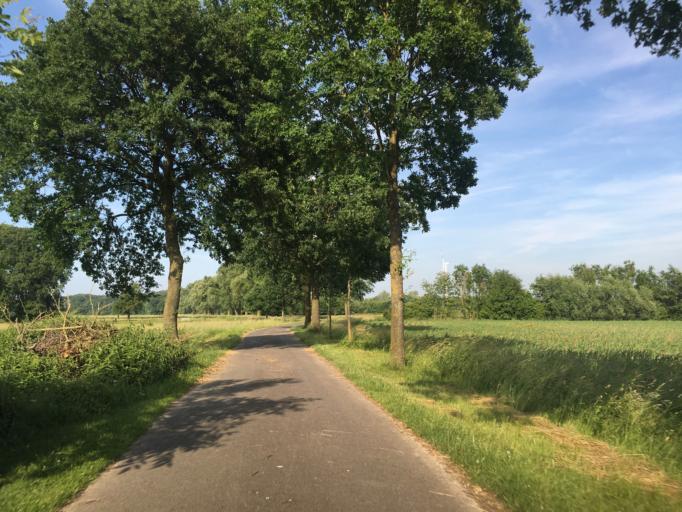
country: DE
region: North Rhine-Westphalia
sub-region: Regierungsbezirk Munster
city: Greven
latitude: 52.0386
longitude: 7.5536
